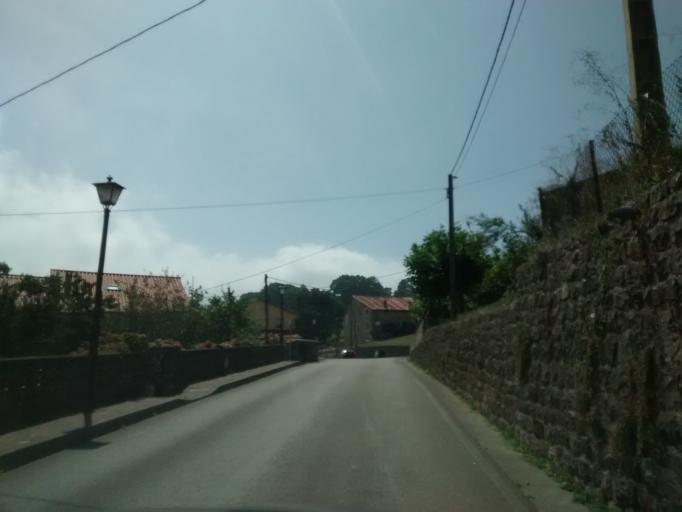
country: ES
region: Cantabria
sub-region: Provincia de Cantabria
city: Ruente
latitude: 43.2650
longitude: -4.2491
